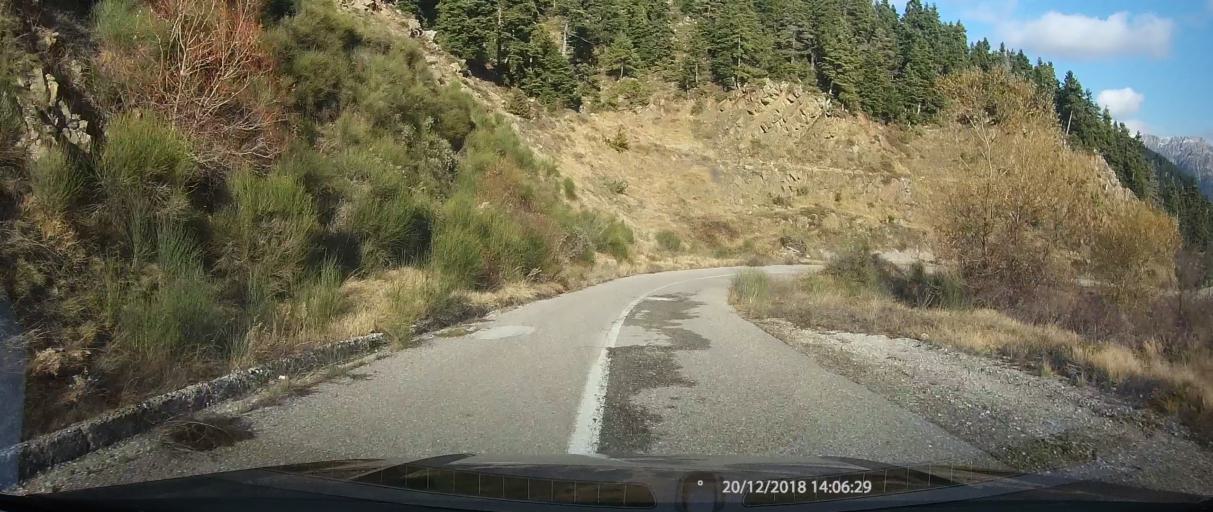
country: GR
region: West Greece
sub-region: Nomos Aitolias kai Akarnanias
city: Thermo
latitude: 38.7519
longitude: 21.6409
